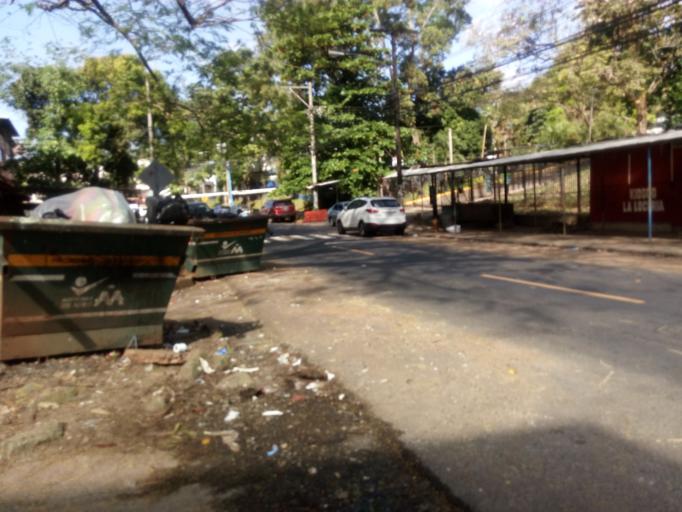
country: PA
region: Panama
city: Panama
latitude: 8.9933
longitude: -79.5364
